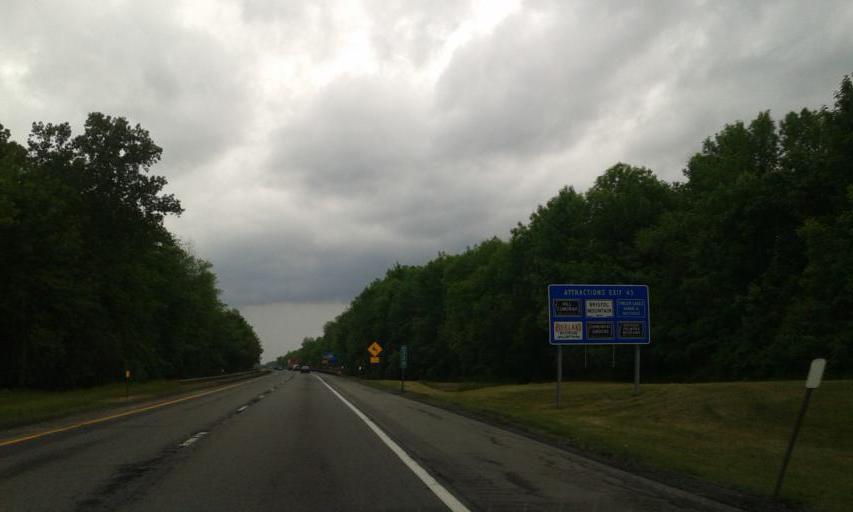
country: US
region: New York
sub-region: Ontario County
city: Manchester
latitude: 42.9779
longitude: -77.2094
